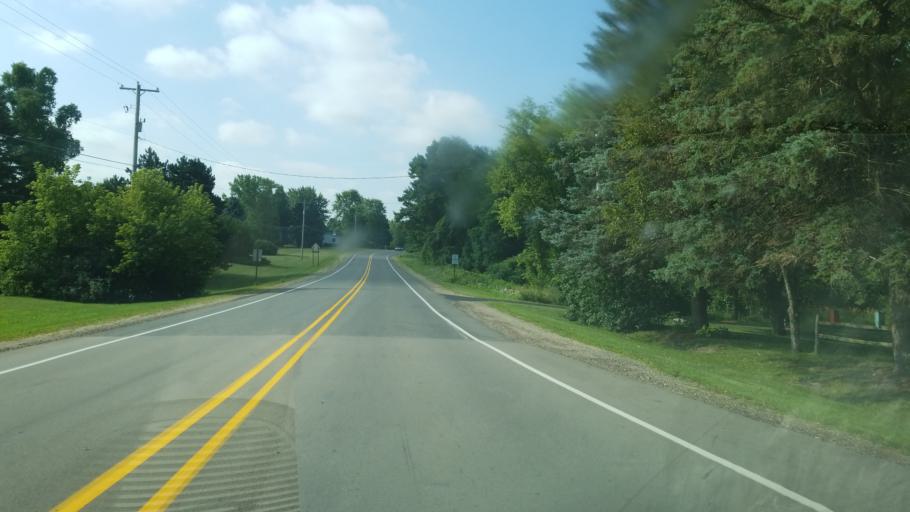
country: US
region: Michigan
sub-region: Kent County
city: Northview
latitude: 43.0939
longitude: -85.6390
